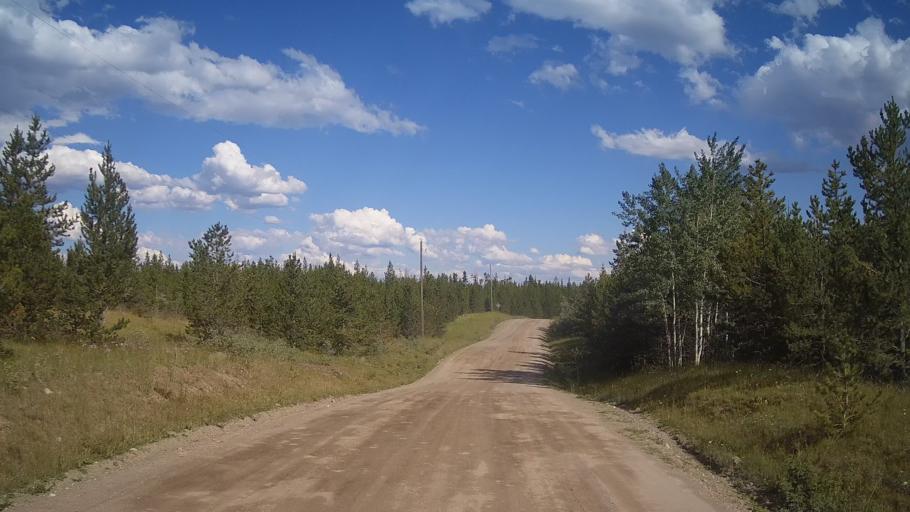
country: CA
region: British Columbia
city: Cache Creek
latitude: 51.2826
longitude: -121.7404
